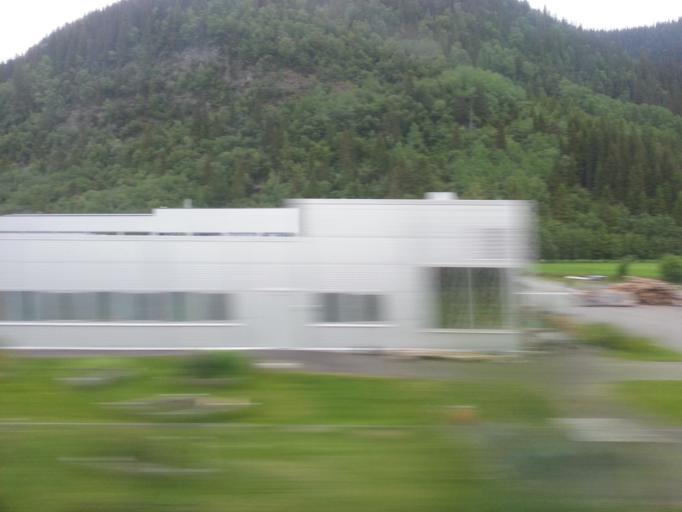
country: NO
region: Sor-Trondelag
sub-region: Melhus
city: Melhus
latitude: 63.2648
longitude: 10.2905
